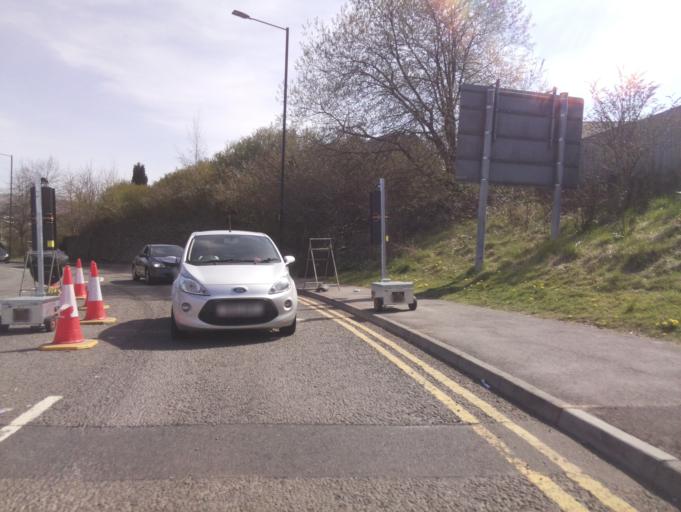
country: GB
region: Wales
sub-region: Merthyr Tydfil County Borough
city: Merthyr Tydfil
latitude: 51.7501
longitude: -3.3881
